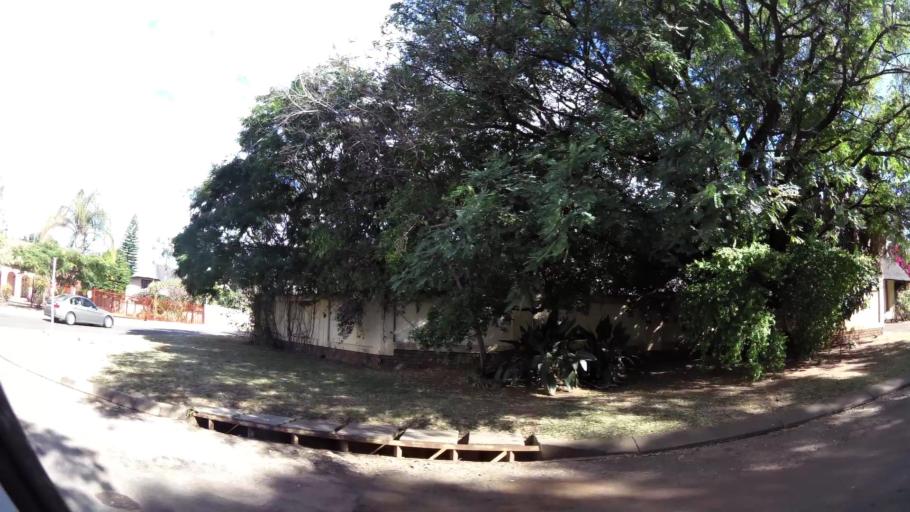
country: ZA
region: Limpopo
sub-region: Waterberg District Municipality
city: Warmbaths
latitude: -24.8734
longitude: 28.2891
